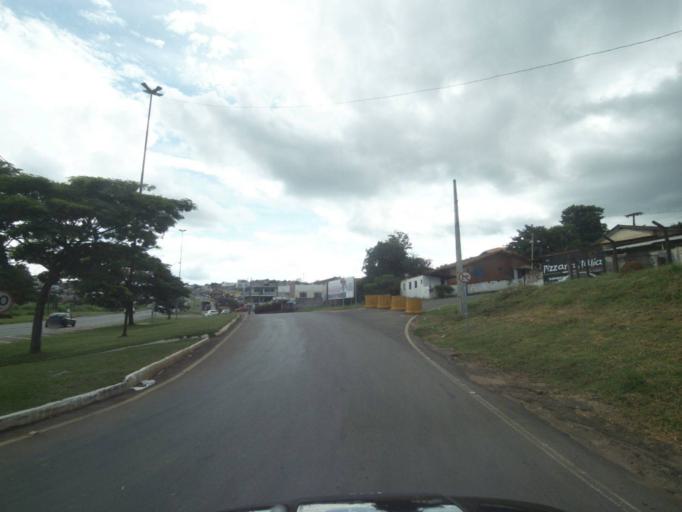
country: BR
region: Parana
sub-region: Telemaco Borba
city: Telemaco Borba
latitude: -24.3262
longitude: -50.6314
